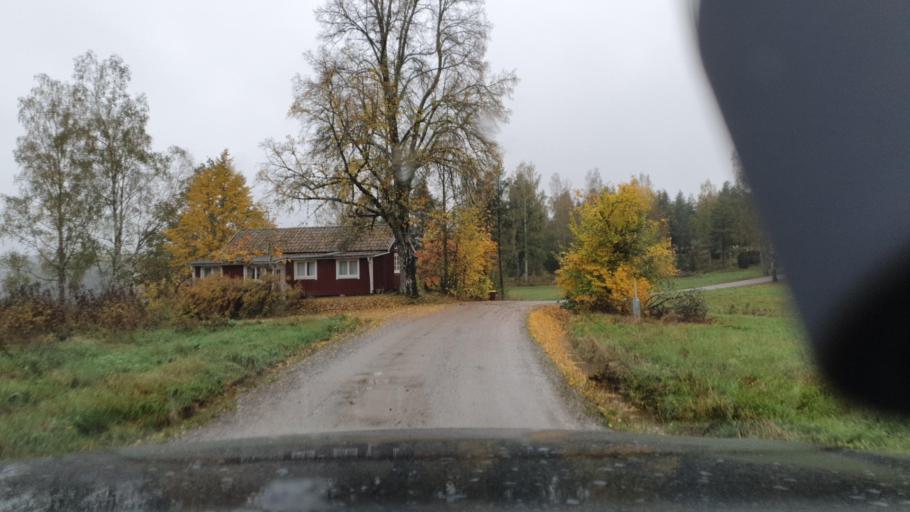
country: SE
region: Vaermland
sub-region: Karlstads Kommun
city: Edsvalla
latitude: 59.6006
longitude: 12.9210
